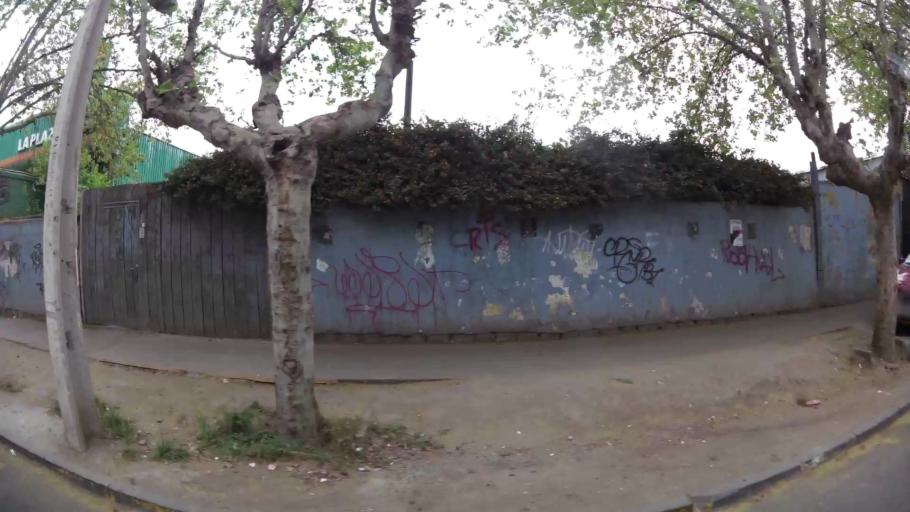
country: CL
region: Santiago Metropolitan
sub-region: Provincia de Chacabuco
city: Chicureo Abajo
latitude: -33.2024
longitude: -70.6753
